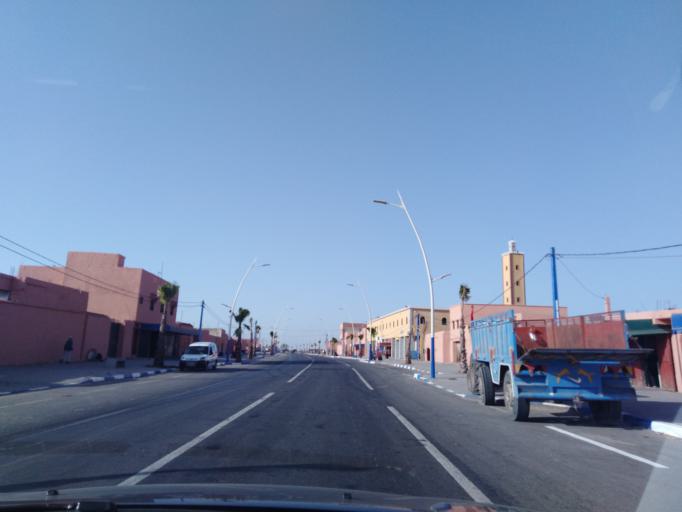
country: MA
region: Doukkala-Abda
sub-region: El-Jadida
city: Sidi Bennour
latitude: 32.5826
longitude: -8.7128
